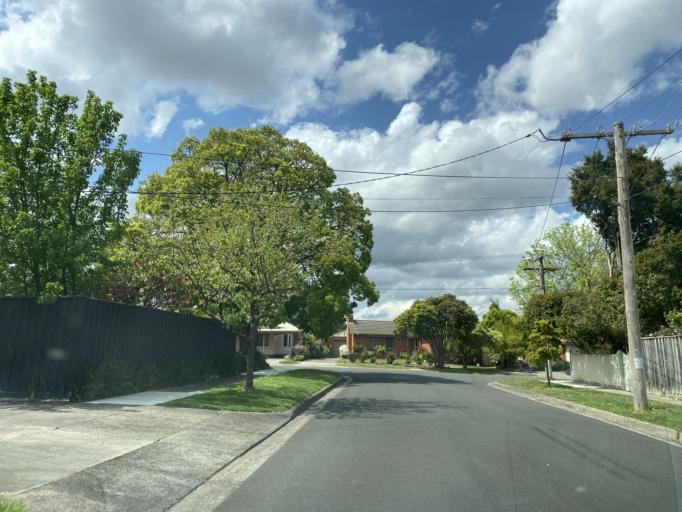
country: AU
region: Victoria
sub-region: Whitehorse
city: Burwood
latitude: -37.8599
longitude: 145.1277
